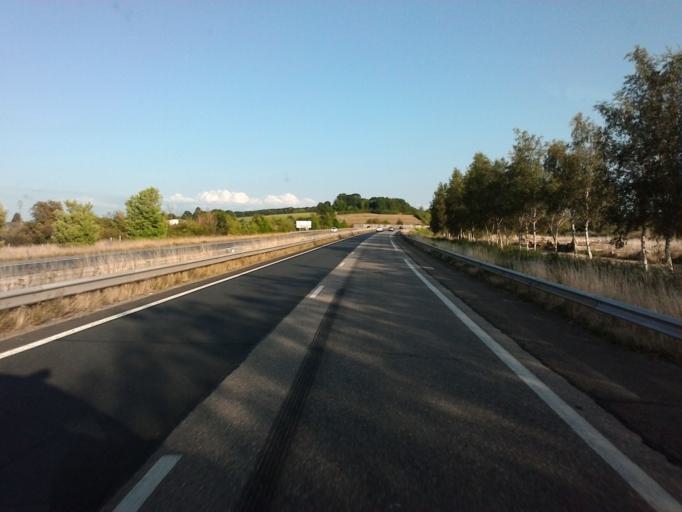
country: FR
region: Lorraine
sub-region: Departement des Vosges
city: Dogneville
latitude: 48.2217
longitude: 6.4501
